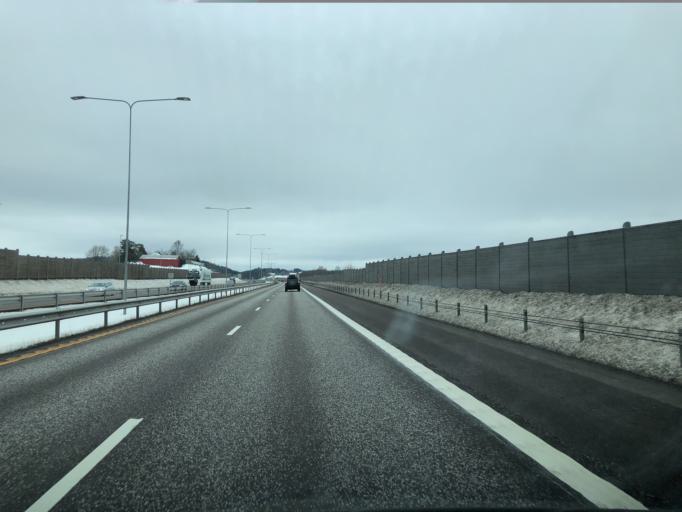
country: NO
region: Vestfold
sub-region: Horten
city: Skoppum
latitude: 59.4101
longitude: 10.3639
